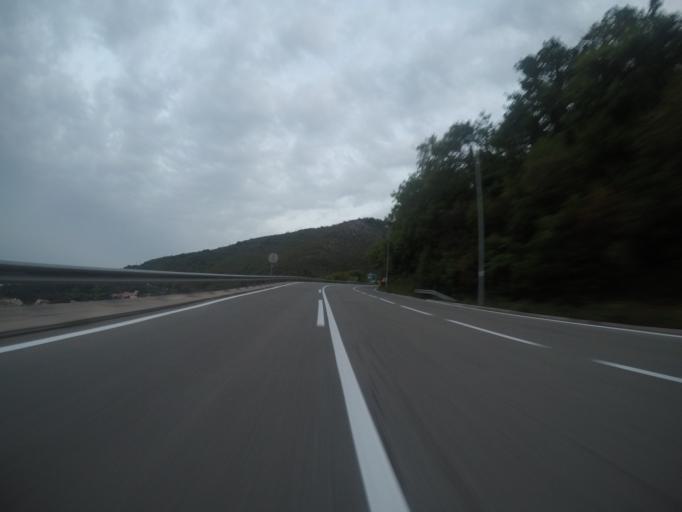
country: ME
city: Petrovac na Moru
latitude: 42.2091
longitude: 18.9469
